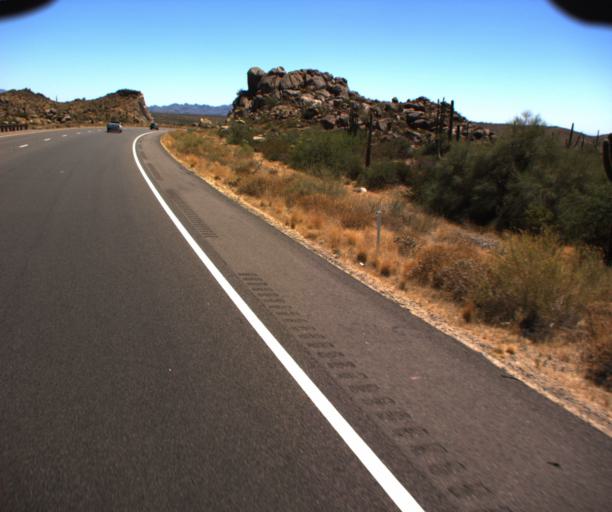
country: US
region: Arizona
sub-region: Maricopa County
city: Rio Verde
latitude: 33.6976
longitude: -111.5020
